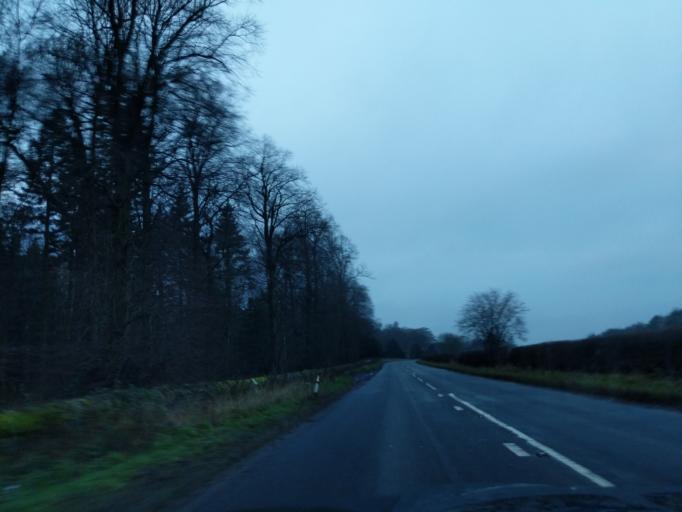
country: GB
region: England
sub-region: Northumberland
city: Stannington
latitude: 55.0889
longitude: -1.6558
